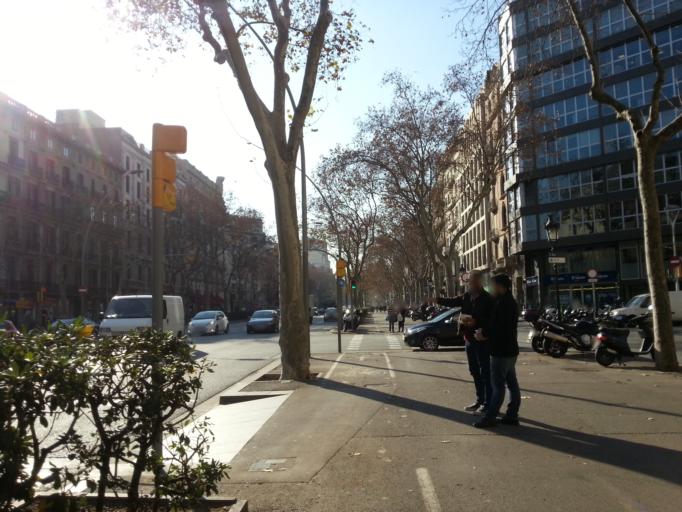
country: ES
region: Catalonia
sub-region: Provincia de Barcelona
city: Eixample
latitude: 41.3926
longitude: 2.1723
